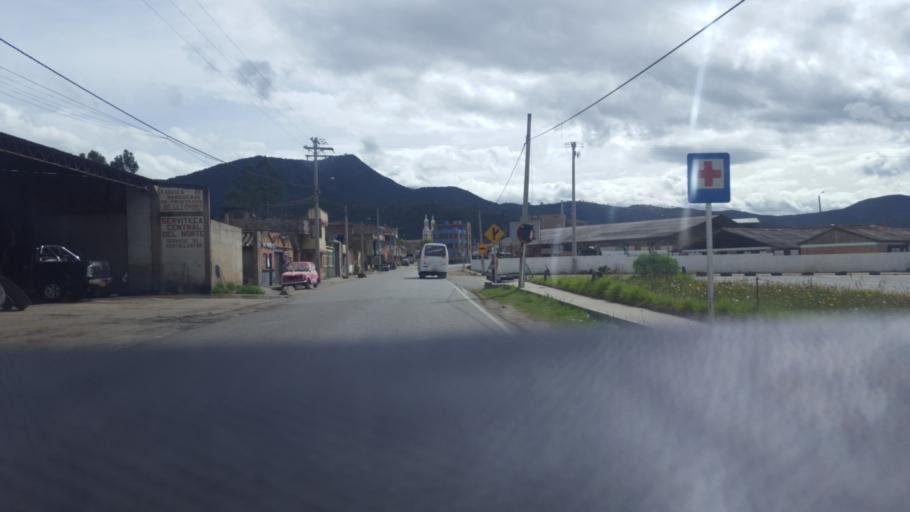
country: CO
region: Boyaca
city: Belen
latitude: 5.9853
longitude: -72.9177
